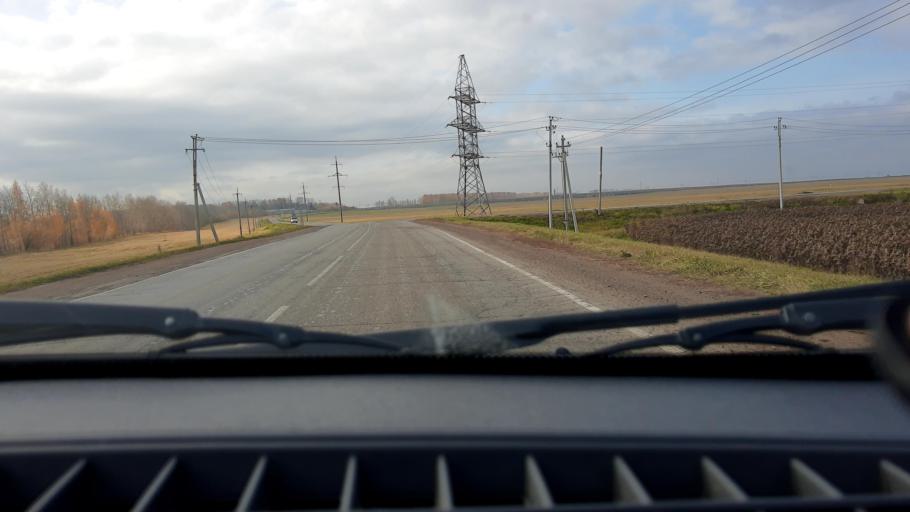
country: RU
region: Bashkortostan
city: Kabakovo
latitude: 54.5374
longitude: 56.0723
